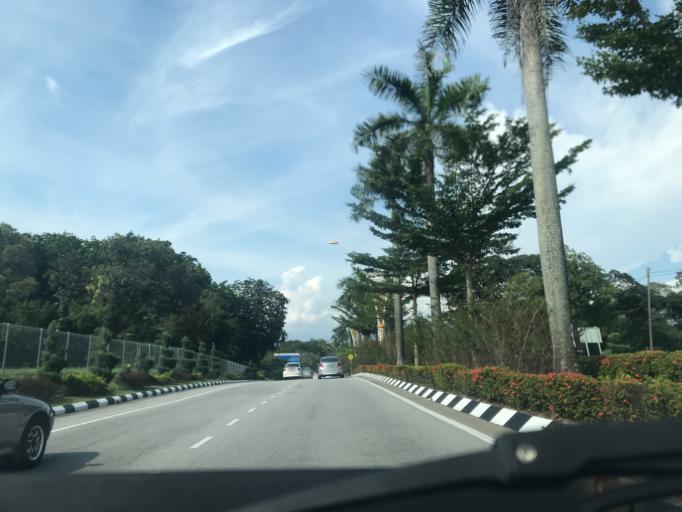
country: MY
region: Perak
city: Ipoh
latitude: 4.5967
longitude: 101.1029
